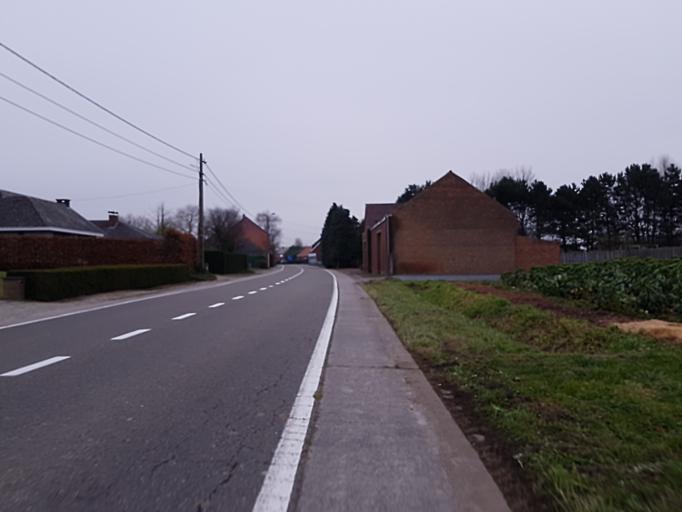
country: BE
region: Flanders
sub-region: Provincie Vlaams-Brabant
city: Kapelle-op-den-Bos
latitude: 51.0337
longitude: 4.3928
